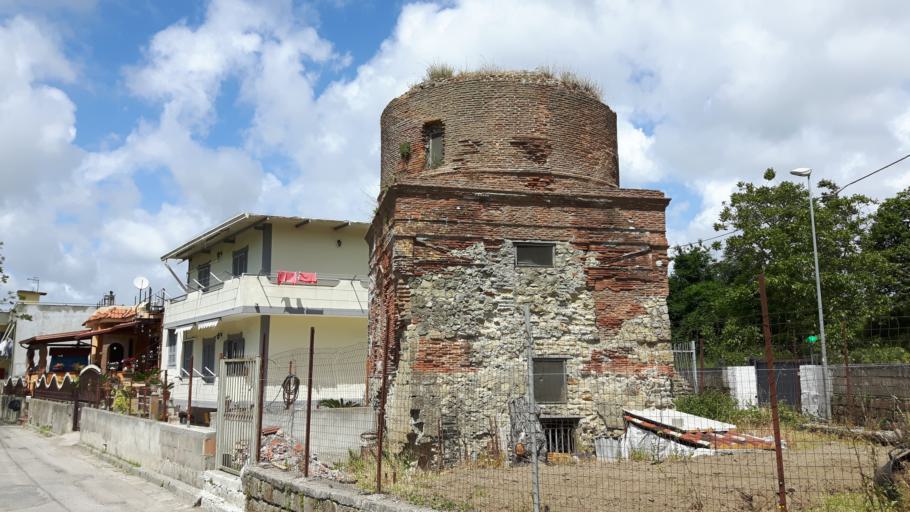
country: IT
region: Campania
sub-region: Provincia di Napoli
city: Quarto
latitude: 40.8464
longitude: 14.1178
